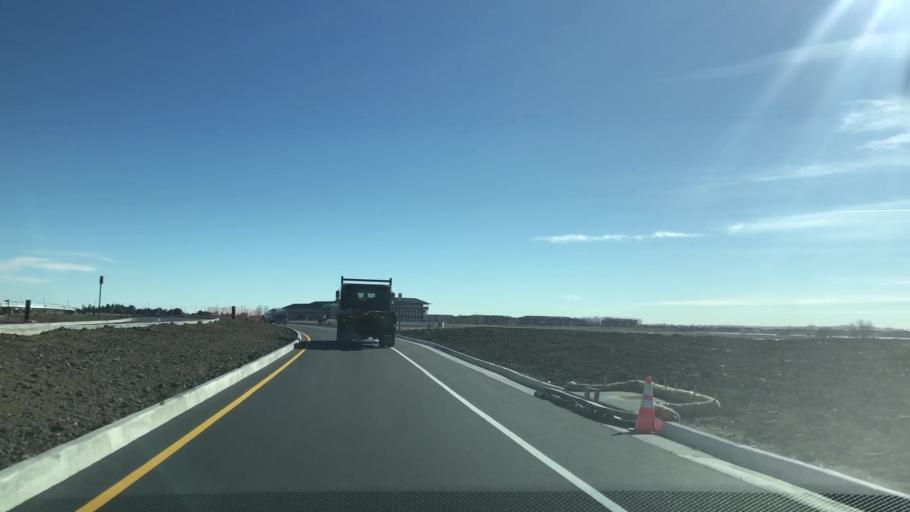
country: US
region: Colorado
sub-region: Larimer County
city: Loveland
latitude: 40.4275
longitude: -105.0085
